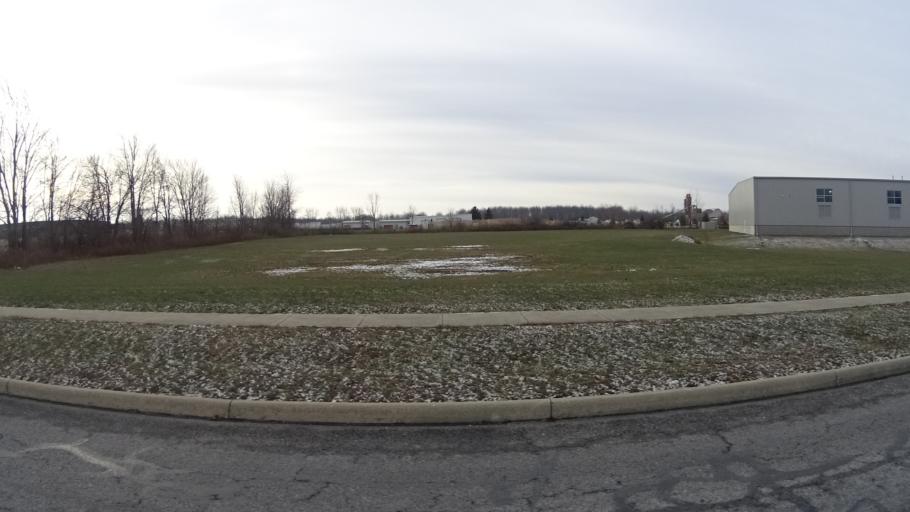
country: US
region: Ohio
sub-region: Lorain County
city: Lagrange
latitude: 41.2313
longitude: -82.1152
